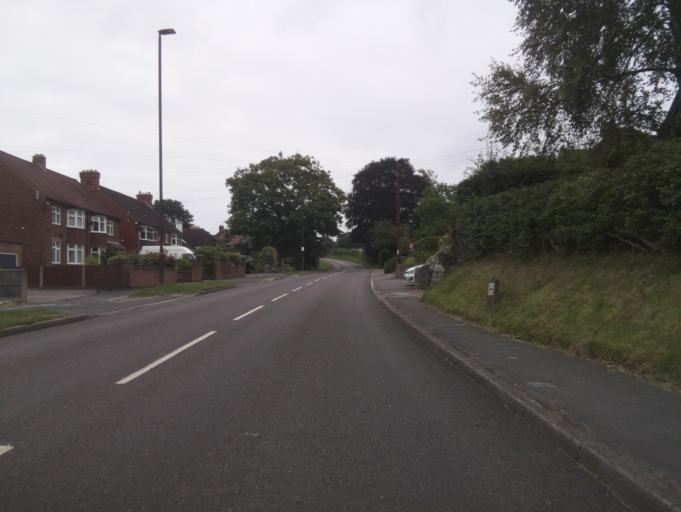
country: GB
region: England
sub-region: Derbyshire
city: Ashbourne
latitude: 53.0136
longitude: -1.7236
